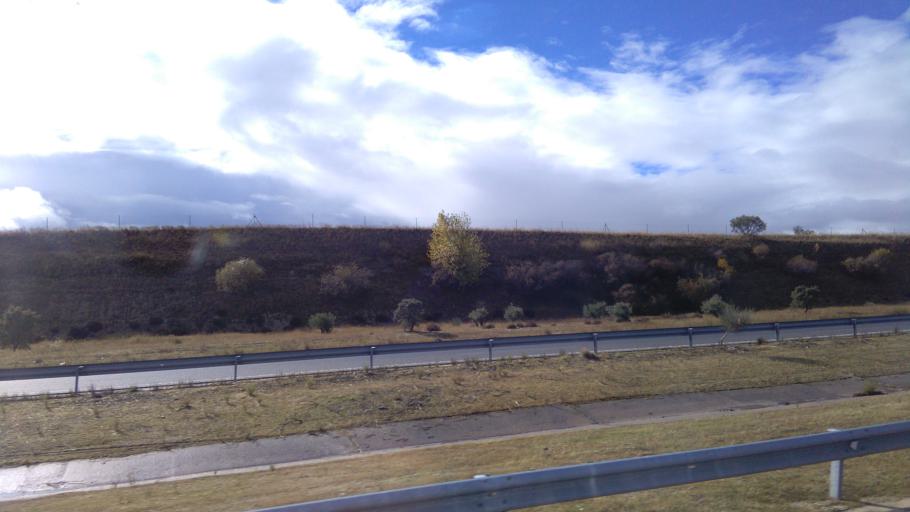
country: ES
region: Madrid
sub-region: Provincia de Madrid
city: Navalcarnero
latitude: 40.2658
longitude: -4.0256
